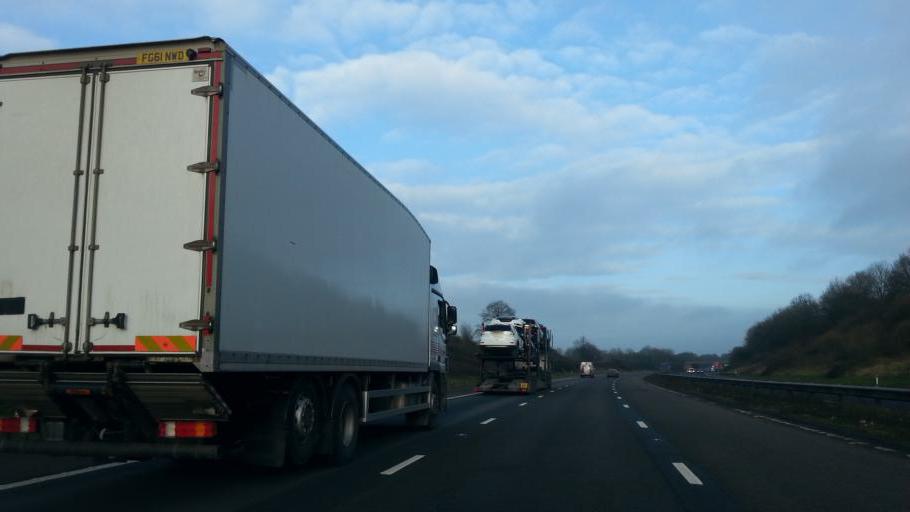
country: GB
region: England
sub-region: Gloucestershire
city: Dursley
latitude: 51.7039
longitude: -2.3883
